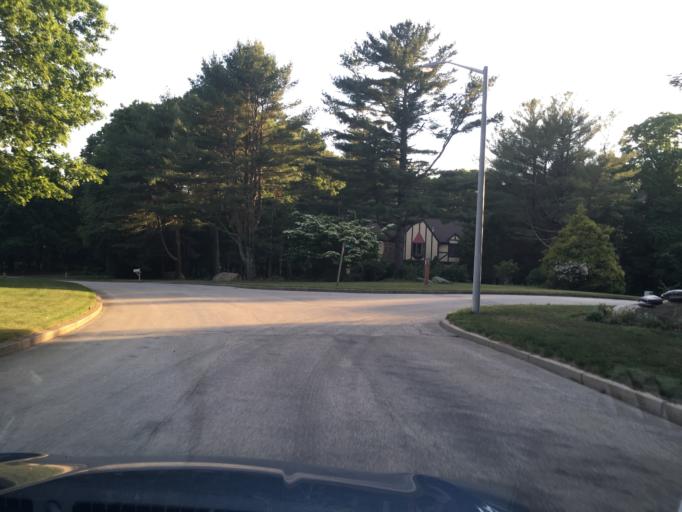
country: US
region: Rhode Island
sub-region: Kent County
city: West Warwick
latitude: 41.6373
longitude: -71.5200
